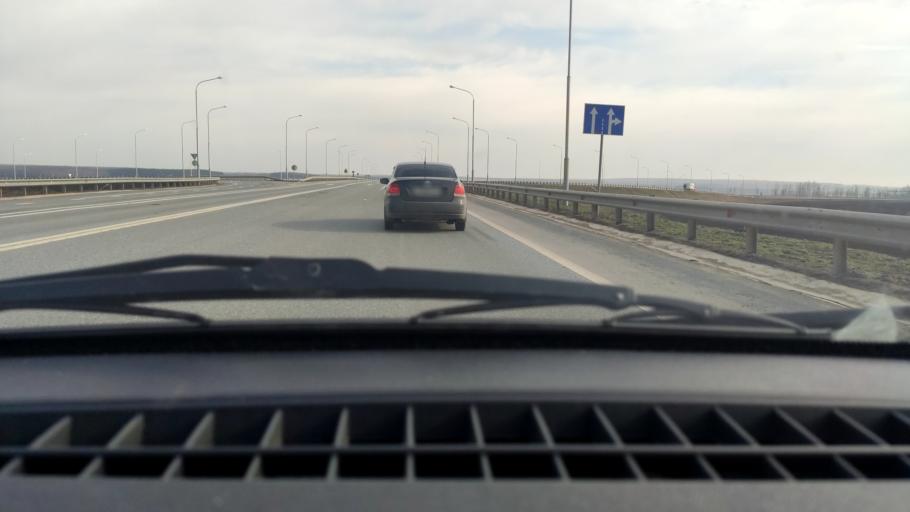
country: RU
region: Bashkortostan
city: Chishmy
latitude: 54.6644
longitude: 55.3978
